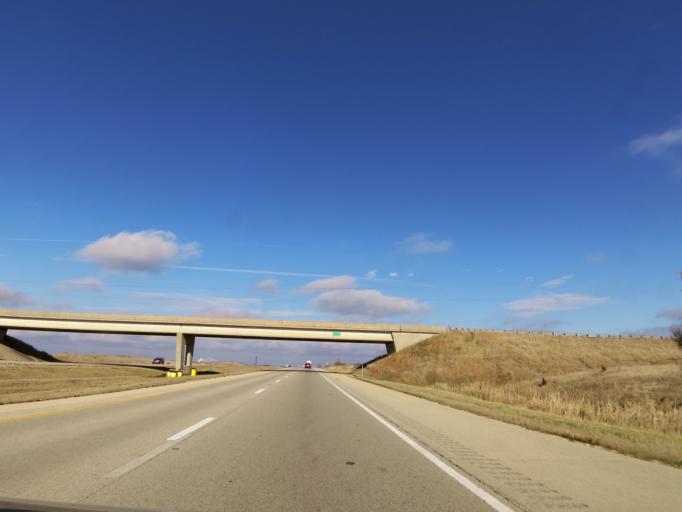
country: US
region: Illinois
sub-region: Ogle County
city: Rochelle
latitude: 41.8176
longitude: -89.0095
